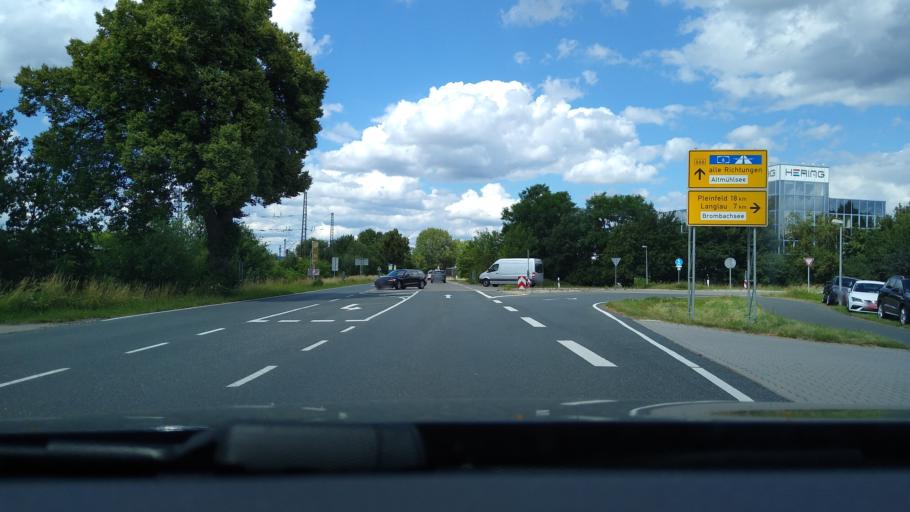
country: DE
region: Bavaria
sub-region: Regierungsbezirk Mittelfranken
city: Gunzenhausen
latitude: 49.1249
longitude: 10.7674
